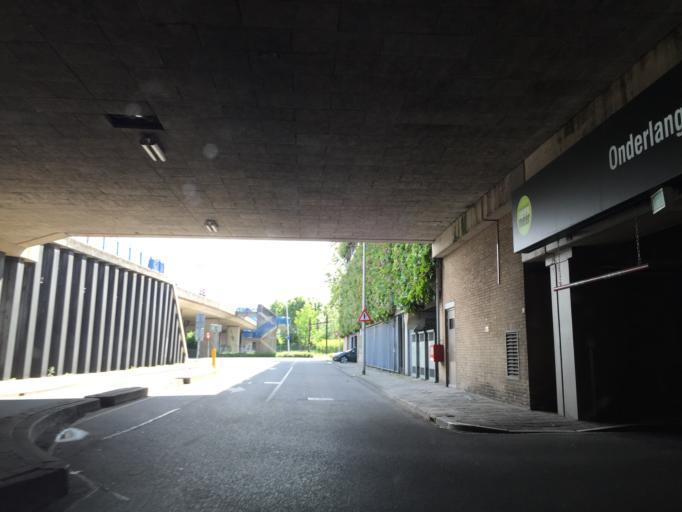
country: NL
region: South Holland
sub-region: Gemeente Zoetermeer
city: Zoetermeer
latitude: 52.0610
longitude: 4.4878
